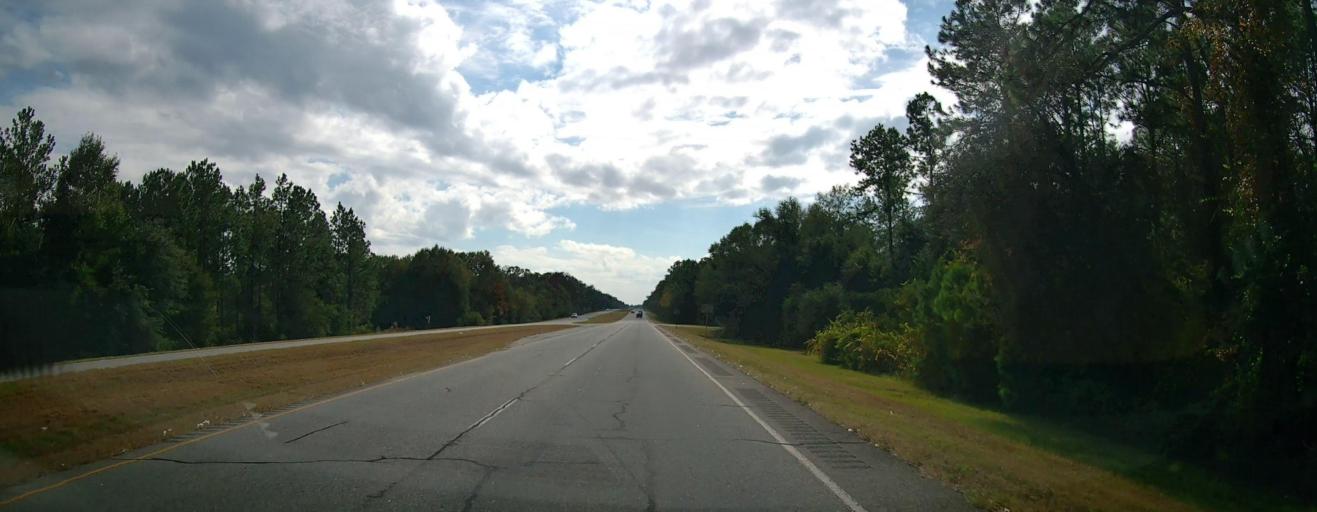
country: US
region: Georgia
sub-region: Mitchell County
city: Camilla
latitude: 31.3104
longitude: -84.1771
